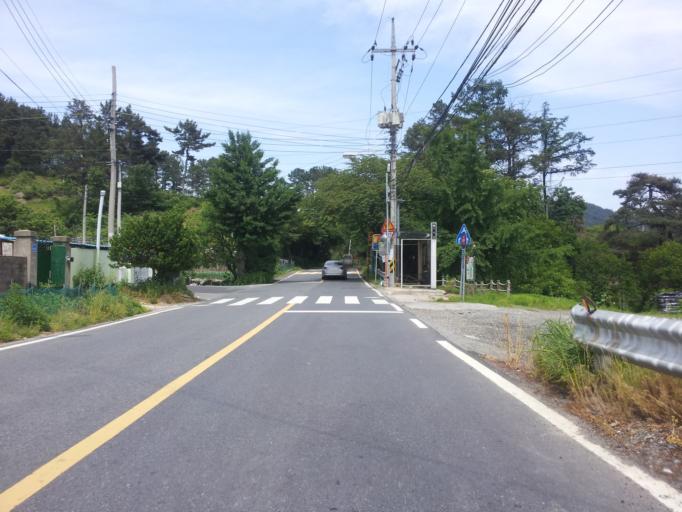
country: KR
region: Daejeon
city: Sintansin
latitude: 36.4275
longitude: 127.4657
